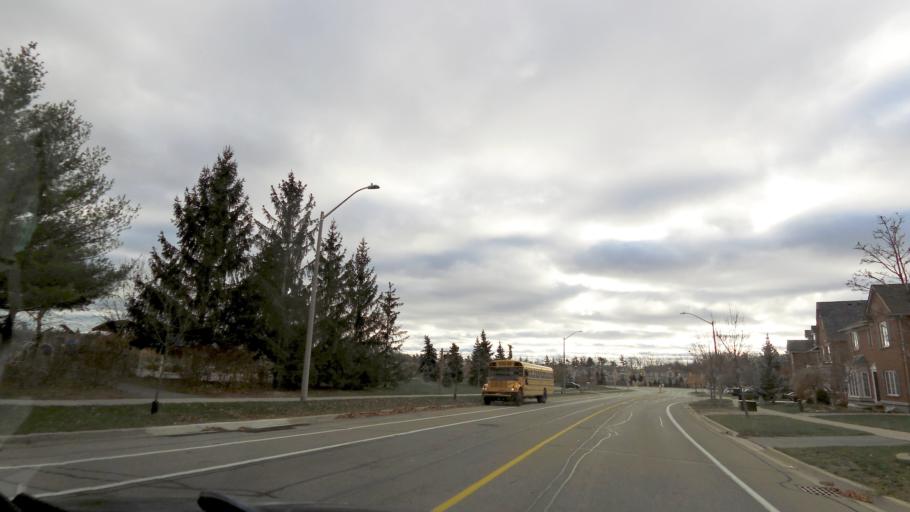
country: CA
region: Ontario
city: Oakville
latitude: 43.4622
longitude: -79.7363
